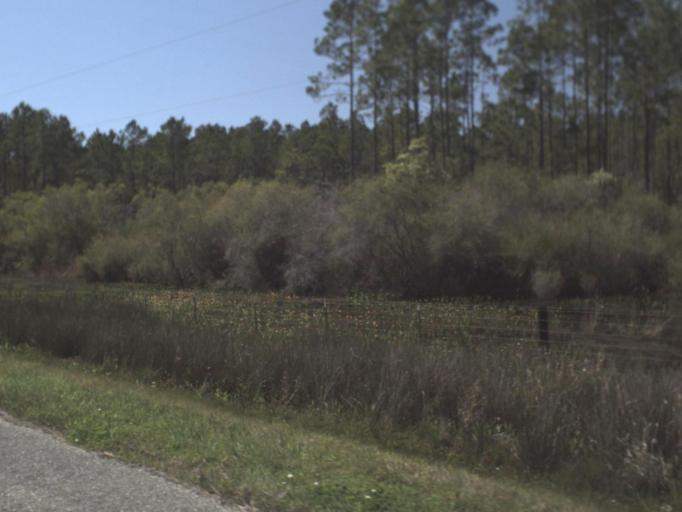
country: US
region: Florida
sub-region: Leon County
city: Woodville
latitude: 30.2132
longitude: -84.0497
